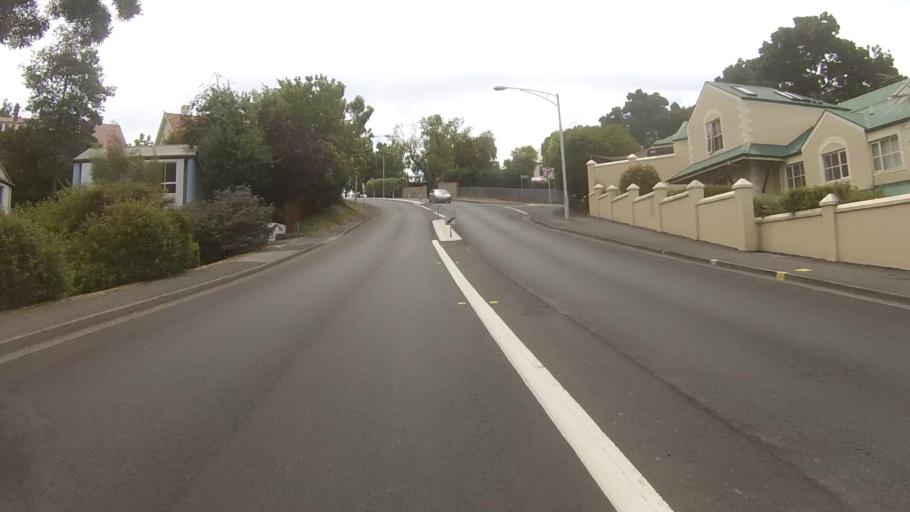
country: AU
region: Tasmania
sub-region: Hobart
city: Sandy Bay
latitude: -42.8932
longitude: 147.3225
